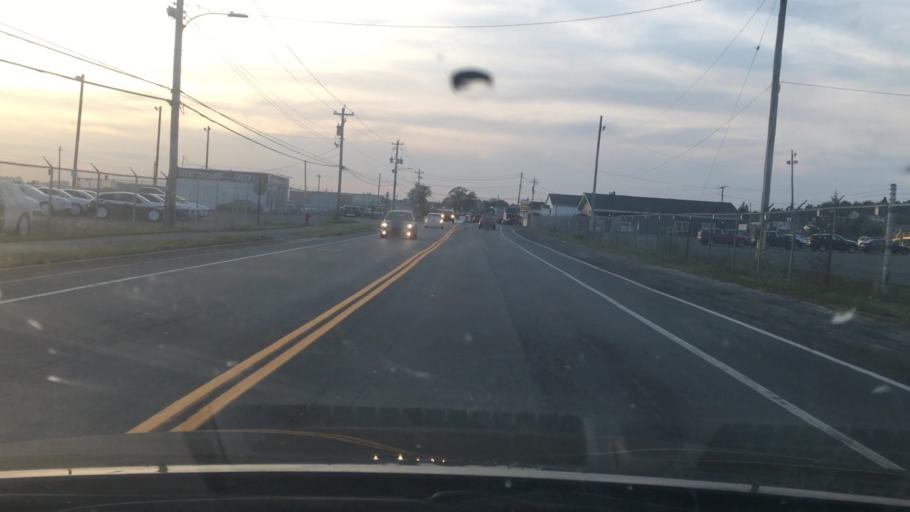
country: CA
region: Nova Scotia
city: Cole Harbour
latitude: 44.6221
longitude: -63.5085
